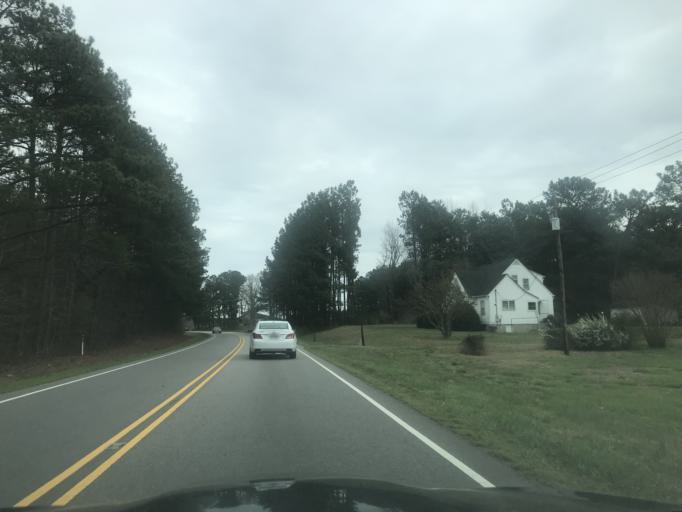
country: US
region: North Carolina
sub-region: Franklin County
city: Louisburg
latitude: 36.0834
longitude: -78.3471
